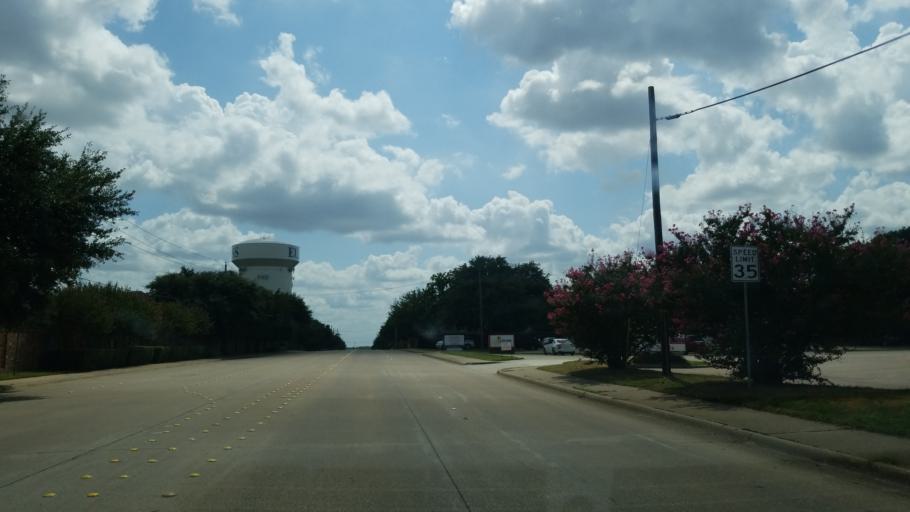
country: US
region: Texas
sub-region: Tarrant County
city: Euless
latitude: 32.8807
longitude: -97.0824
